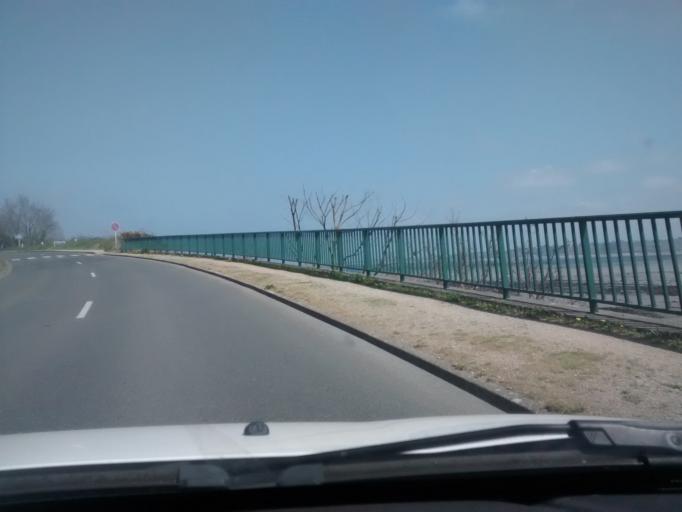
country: FR
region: Brittany
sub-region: Departement des Cotes-d'Armor
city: Perros-Guirec
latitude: 48.8119
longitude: -3.4360
